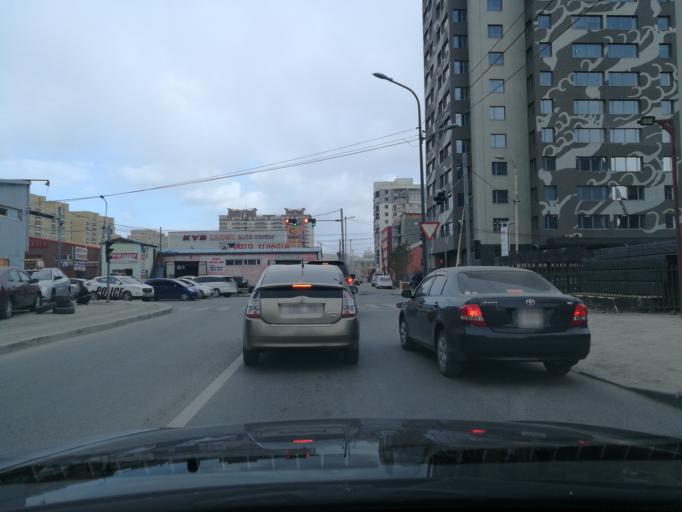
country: MN
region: Ulaanbaatar
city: Ulaanbaatar
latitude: 47.9326
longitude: 106.9159
